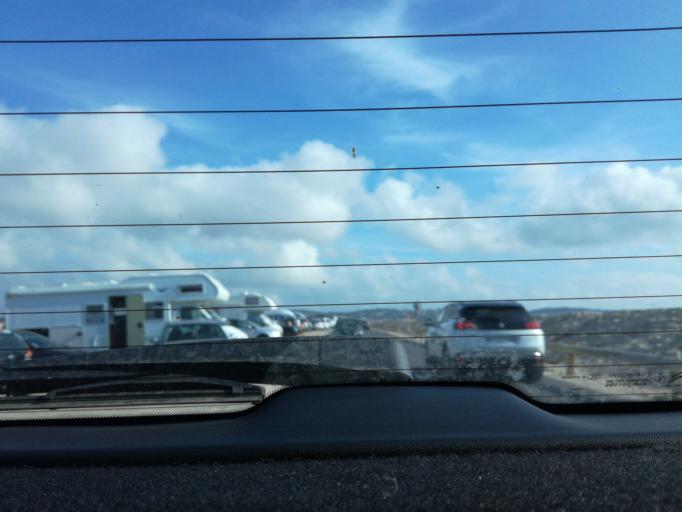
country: FR
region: Provence-Alpes-Cote d'Azur
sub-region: Departement du Var
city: Hyeres
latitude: 43.0682
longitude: 6.1303
